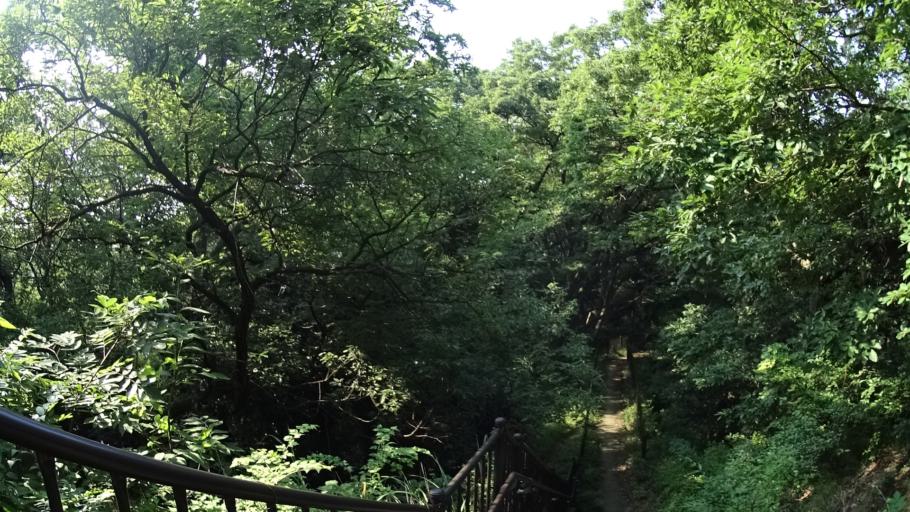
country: JP
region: Kanagawa
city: Zushi
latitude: 35.3052
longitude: 139.6205
